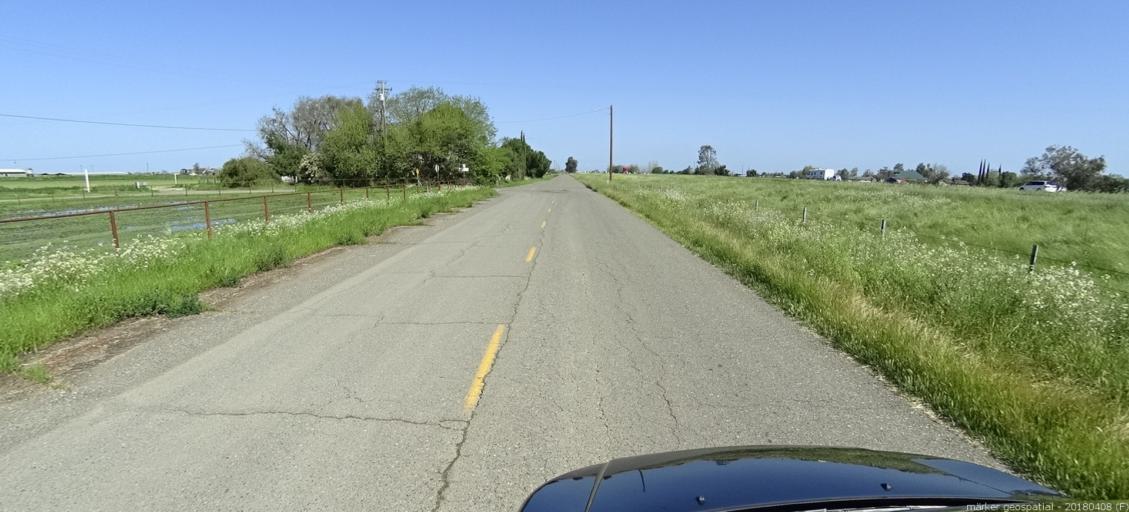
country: US
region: California
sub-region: Sacramento County
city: Walnut Grove
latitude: 38.3275
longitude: -121.4675
